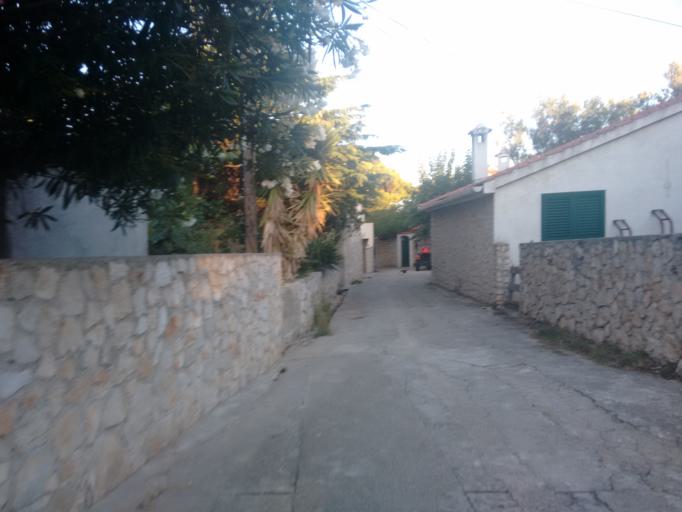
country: HR
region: Licko-Senjska
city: Novalja
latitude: 44.3750
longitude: 14.6968
